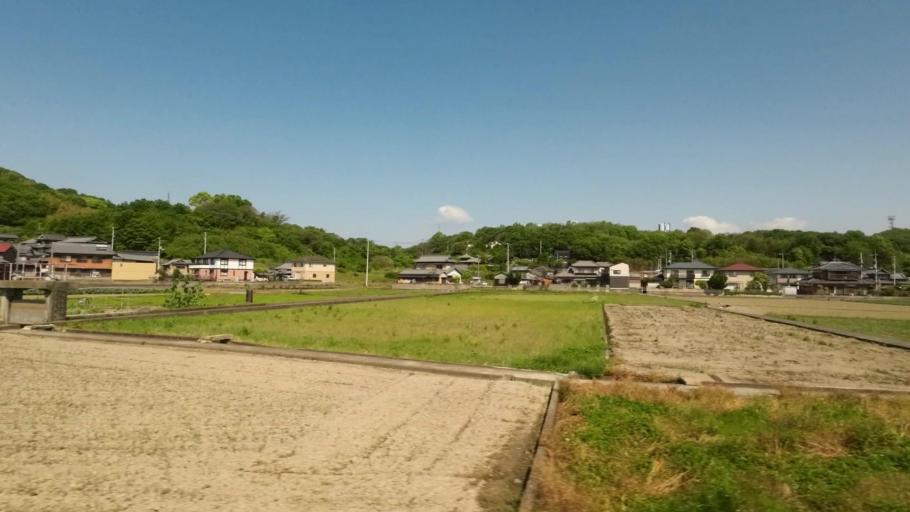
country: JP
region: Kagawa
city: Tadotsu
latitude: 34.2565
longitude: 133.7465
